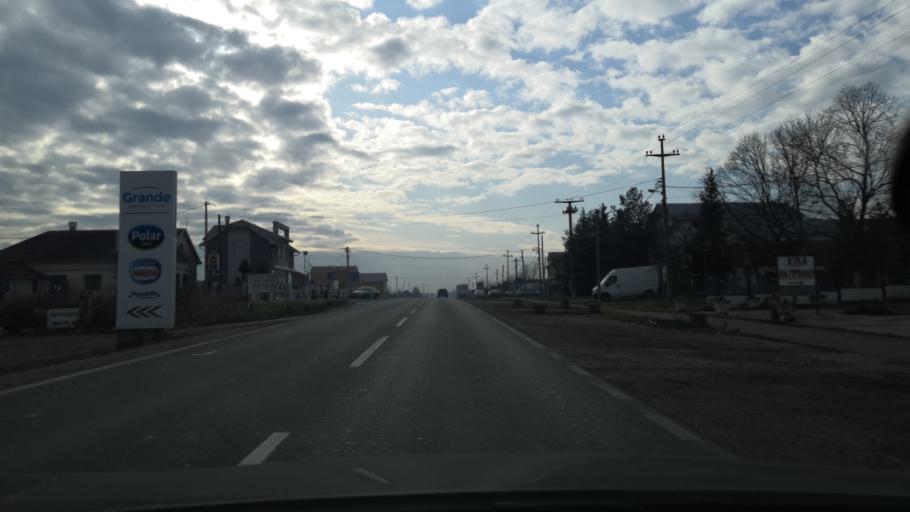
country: RS
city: Ugrinovci
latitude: 44.8678
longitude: 20.2042
